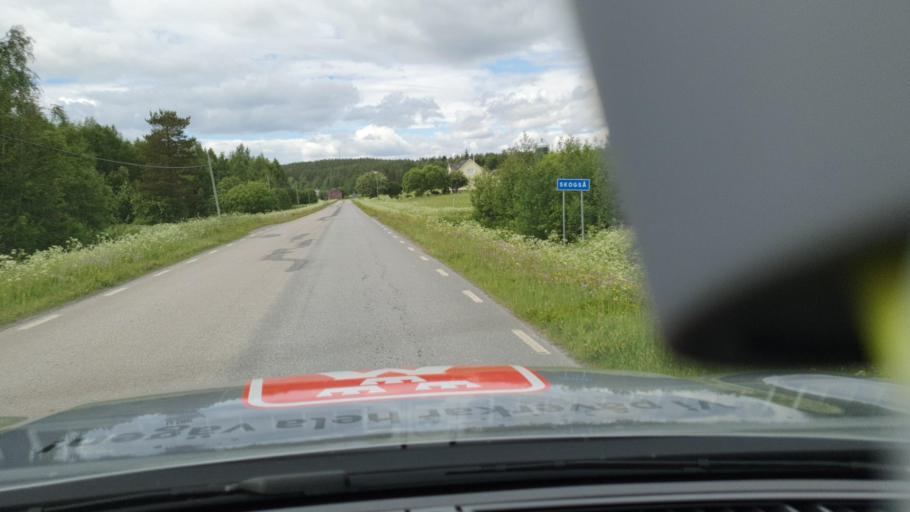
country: SE
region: Norrbotten
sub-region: Bodens Kommun
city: Saevast
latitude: 65.8675
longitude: 21.8984
